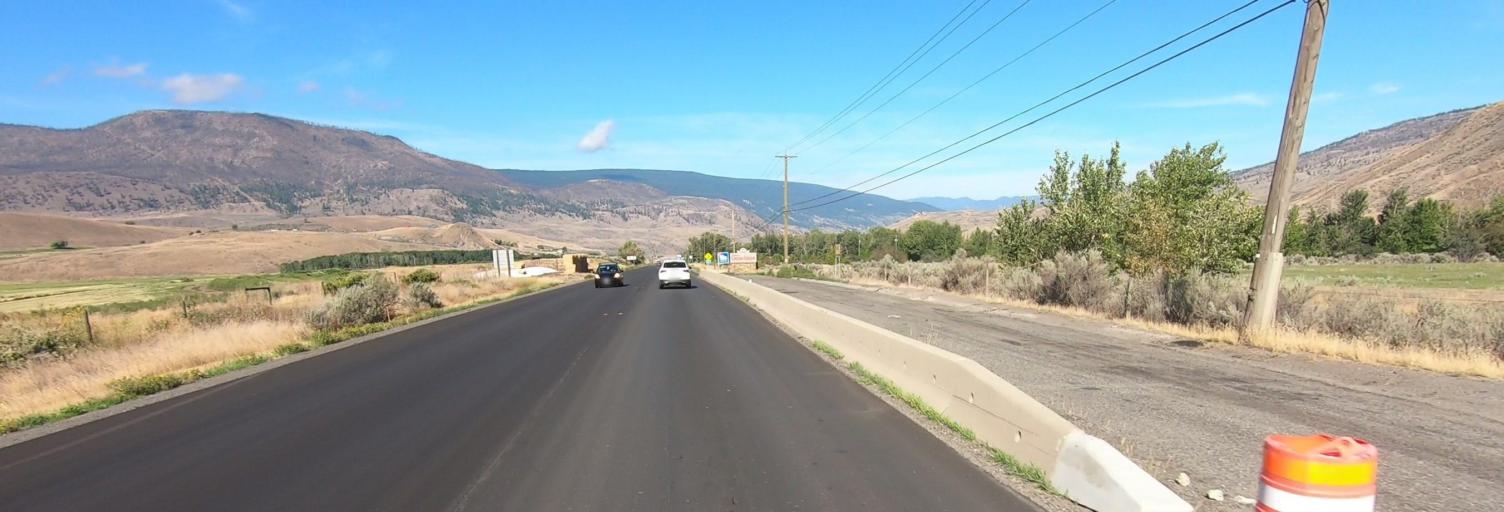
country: CA
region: British Columbia
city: Cache Creek
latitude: 50.8063
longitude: -121.2890
